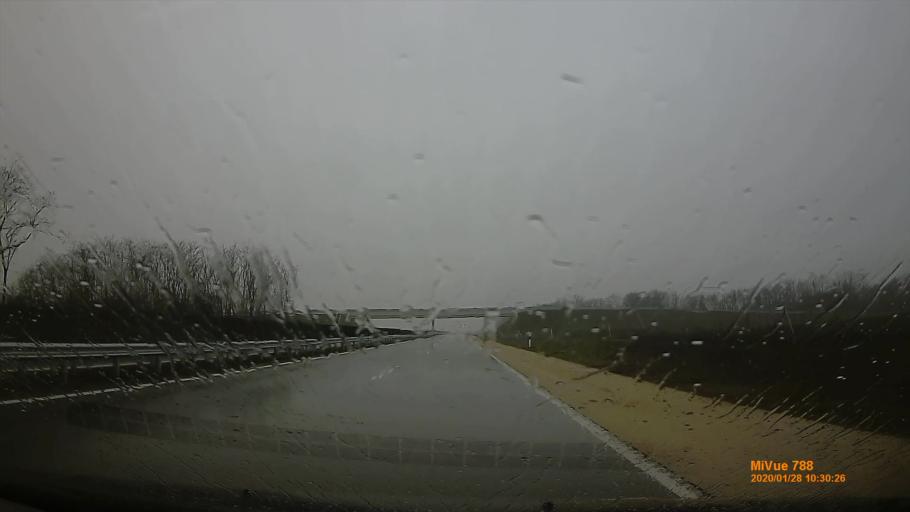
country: HU
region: Pest
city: Gomba
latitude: 47.3317
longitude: 19.5184
